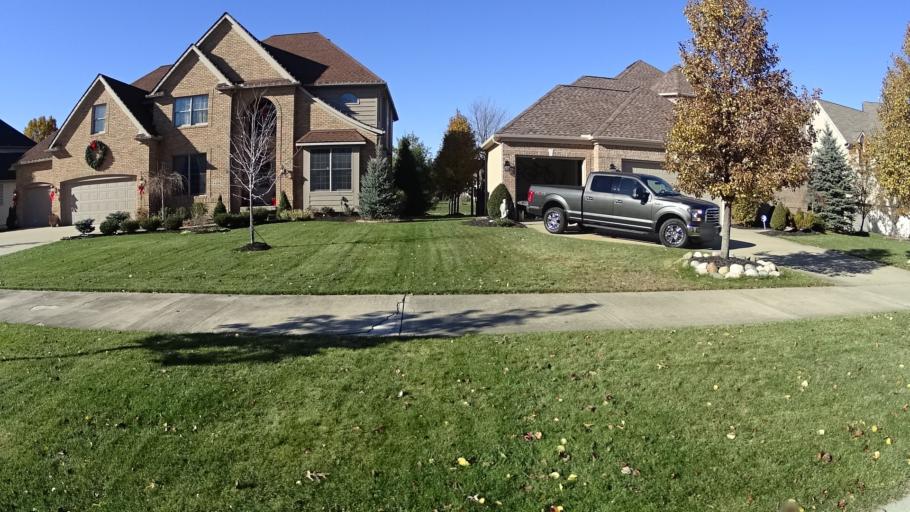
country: US
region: Ohio
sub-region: Lorain County
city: Avon Center
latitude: 41.4262
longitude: -81.9936
